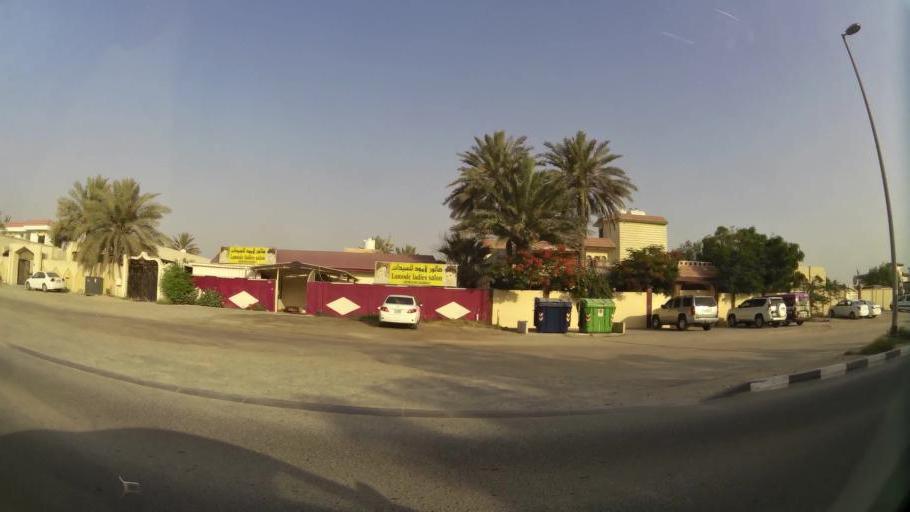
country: AE
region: Ajman
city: Ajman
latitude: 25.3828
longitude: 55.4399
